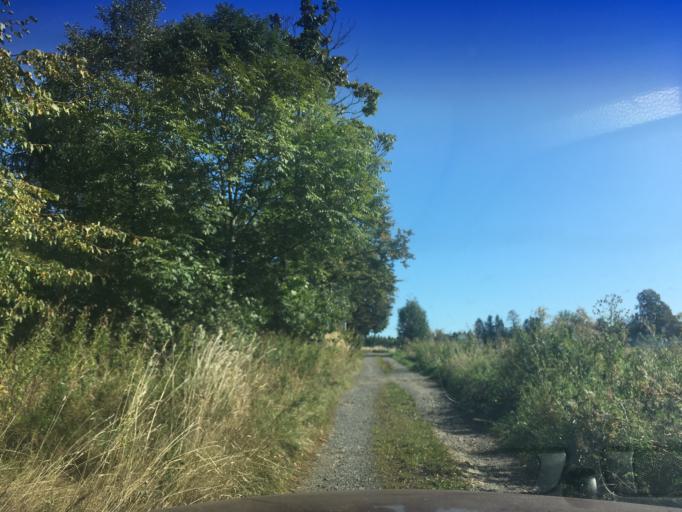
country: PL
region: Lower Silesian Voivodeship
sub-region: Powiat lubanski
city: Lesna
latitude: 50.9779
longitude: 15.3007
